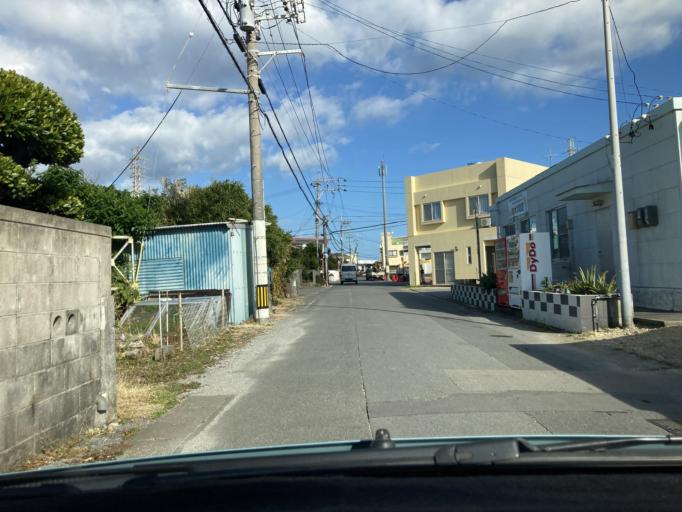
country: JP
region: Okinawa
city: Gushikawa
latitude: 26.3859
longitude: 127.8677
